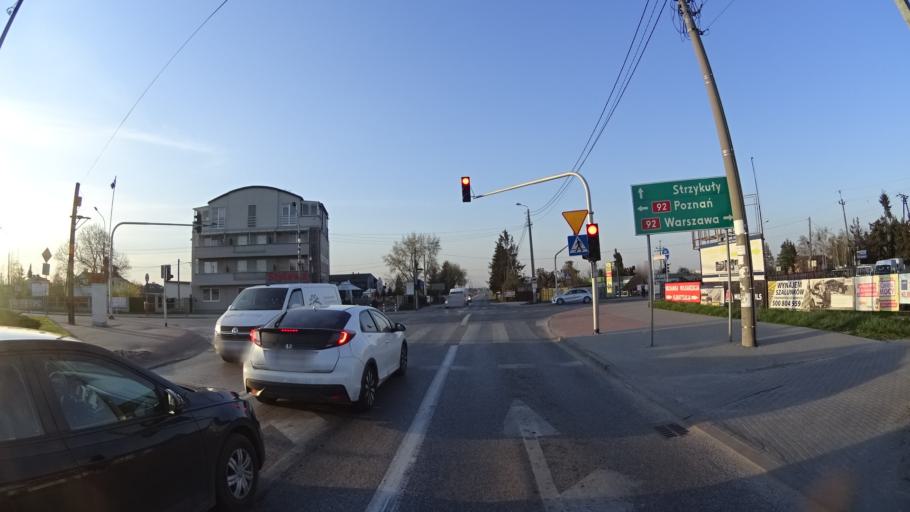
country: PL
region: Masovian Voivodeship
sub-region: Powiat warszawski zachodni
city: Ozarow Mazowiecki
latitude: 52.2097
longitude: 20.8106
